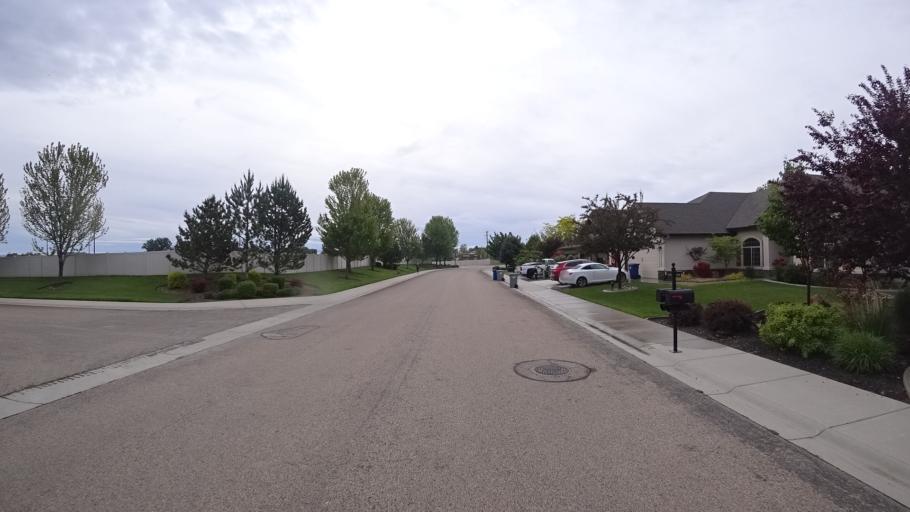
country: US
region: Idaho
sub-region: Ada County
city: Star
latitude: 43.6874
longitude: -116.4997
